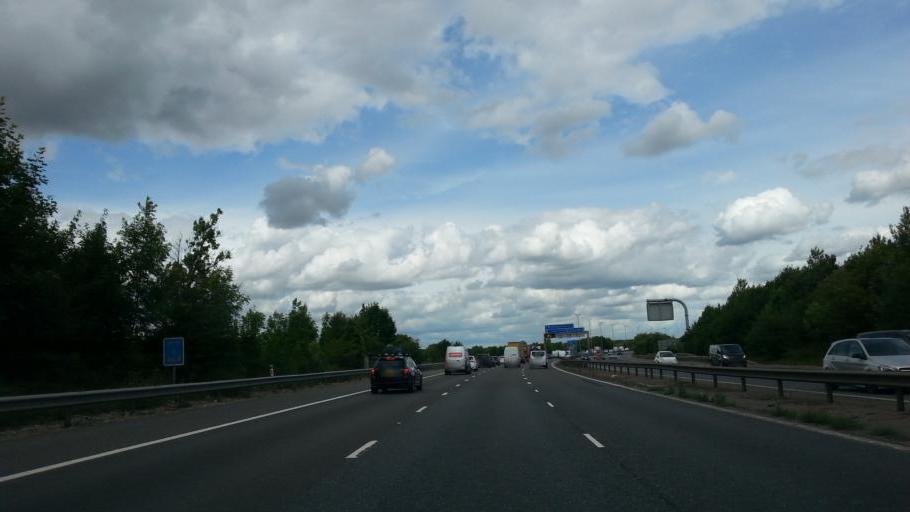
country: GB
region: England
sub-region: Essex
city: Little Hallingbury
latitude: 51.8529
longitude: 0.1846
